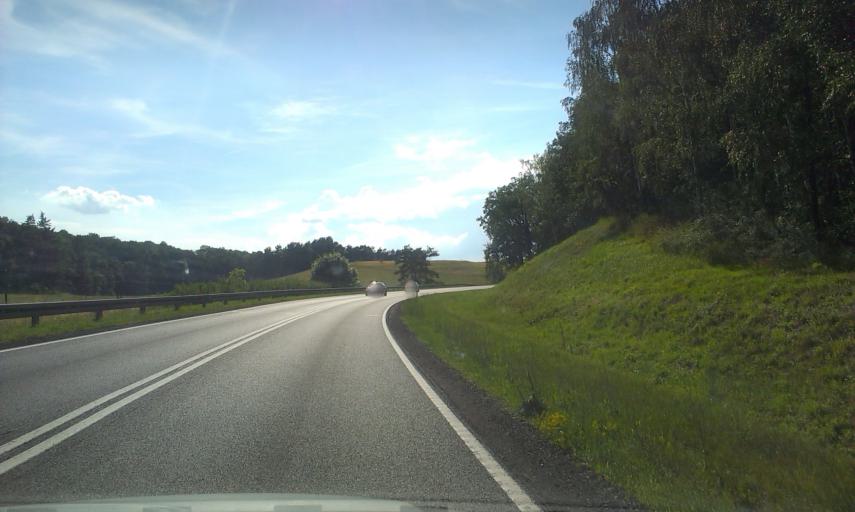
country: PL
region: Kujawsko-Pomorskie
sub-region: Powiat bydgoski
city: Sicienko
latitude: 53.1602
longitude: 17.7990
